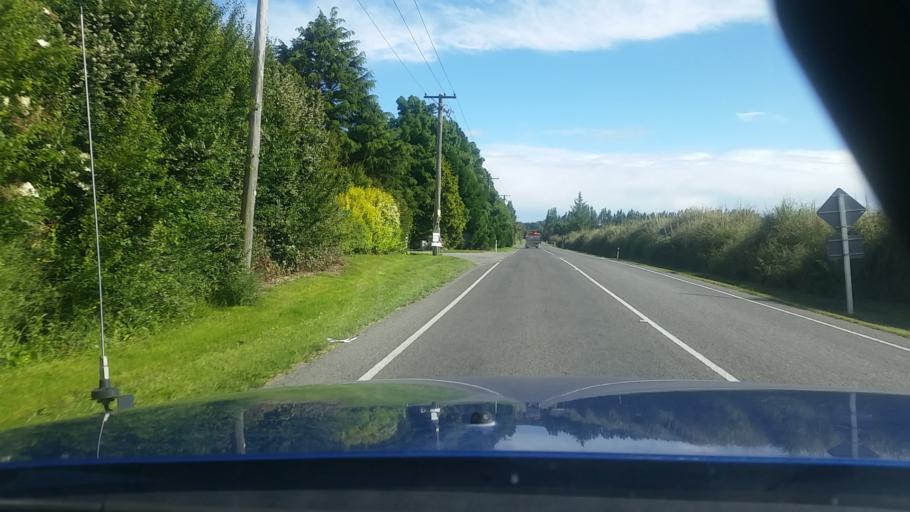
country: NZ
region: Canterbury
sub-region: Ashburton District
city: Ashburton
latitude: -43.8741
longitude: 171.7276
